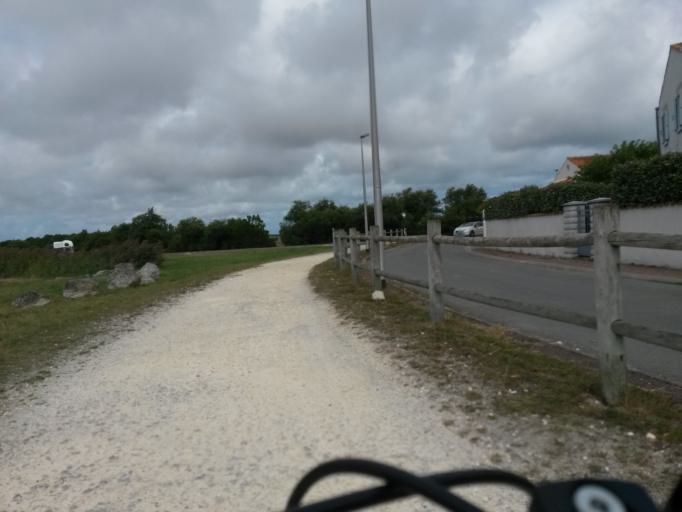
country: FR
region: Poitou-Charentes
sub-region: Departement de la Charente-Maritime
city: Dolus-d'Oleron
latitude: 45.9375
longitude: -1.2762
